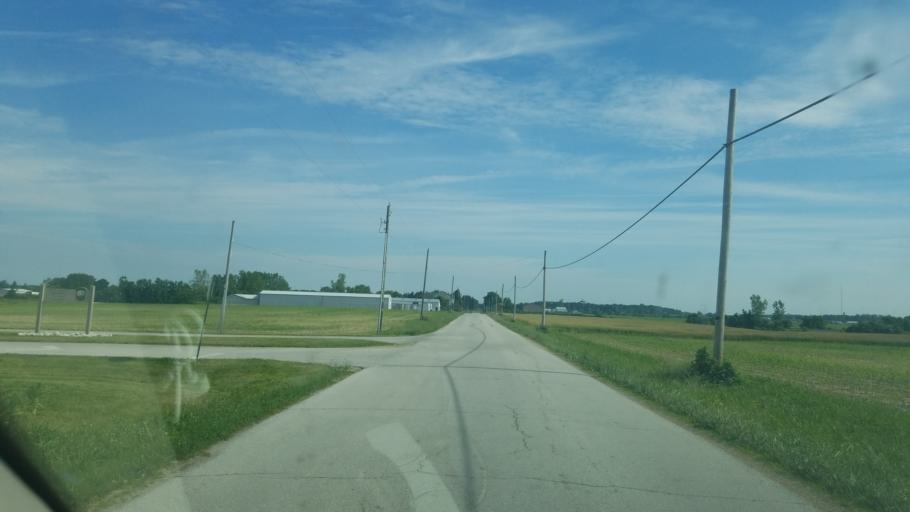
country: US
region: Ohio
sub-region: Wyandot County
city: Upper Sandusky
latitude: 40.8204
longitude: -83.2463
